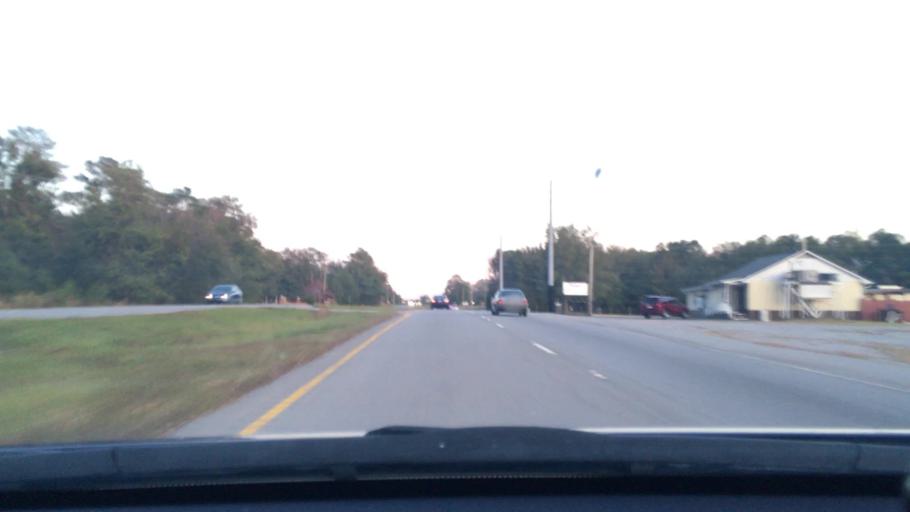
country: US
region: South Carolina
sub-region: Richland County
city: Gadsden
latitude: 33.9417
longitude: -80.7237
